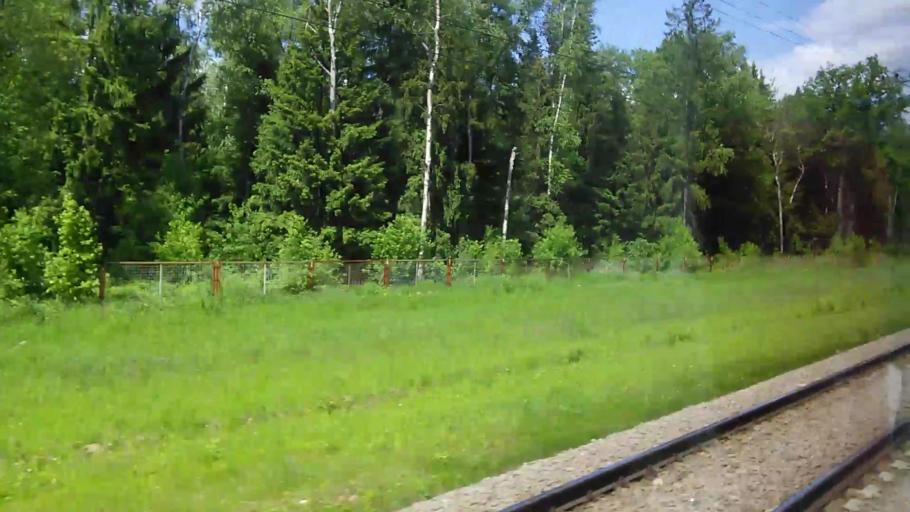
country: RU
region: Moskovskaya
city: Lobnya
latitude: 55.9918
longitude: 37.4738
